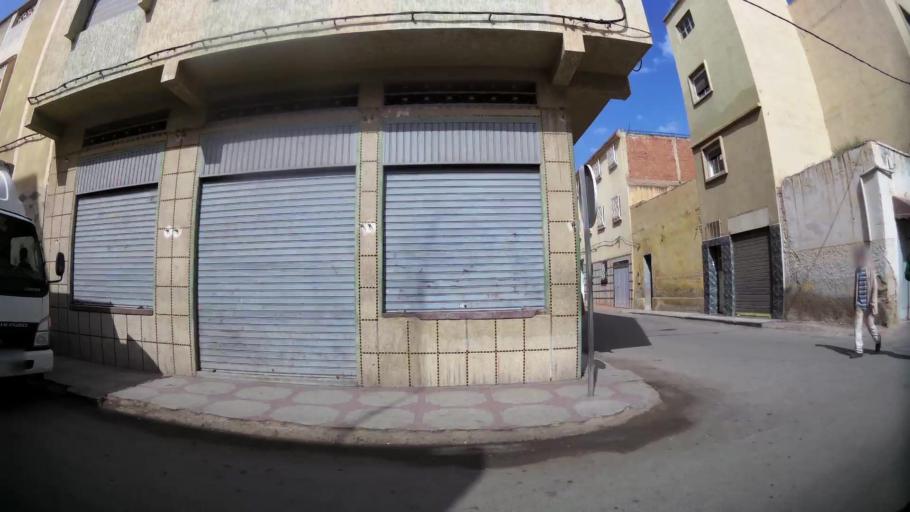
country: MA
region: Oriental
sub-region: Oujda-Angad
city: Oujda
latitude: 34.6867
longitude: -1.9066
